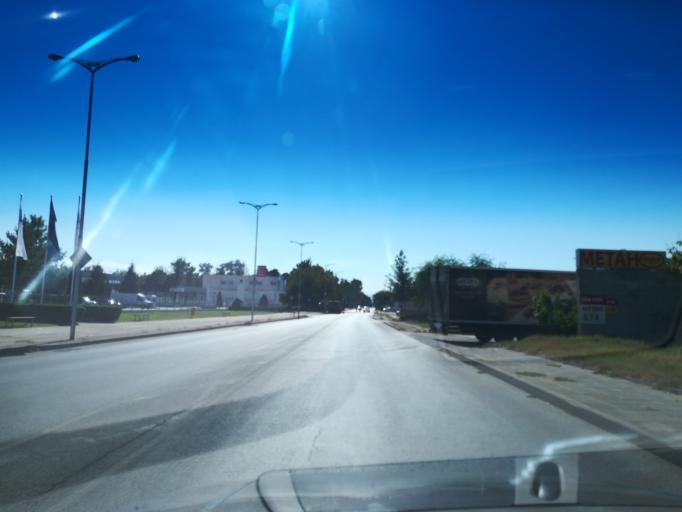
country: BG
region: Plovdiv
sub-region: Obshtina Plovdiv
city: Plovdiv
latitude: 42.1558
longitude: 24.7123
